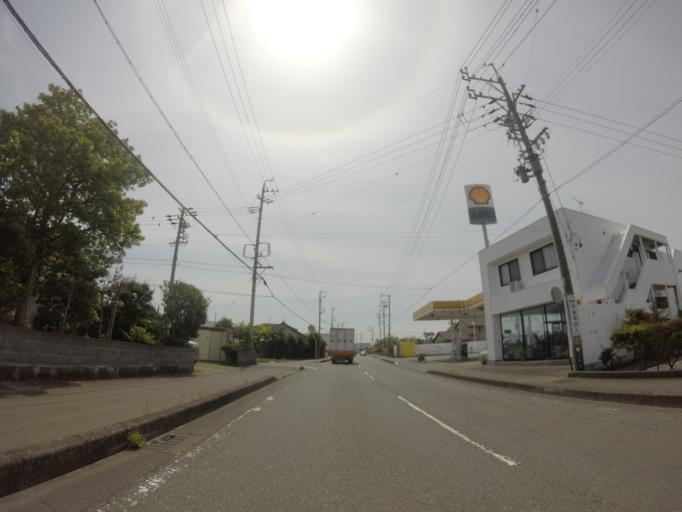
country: JP
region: Shizuoka
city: Fujieda
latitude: 34.7986
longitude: 138.2938
